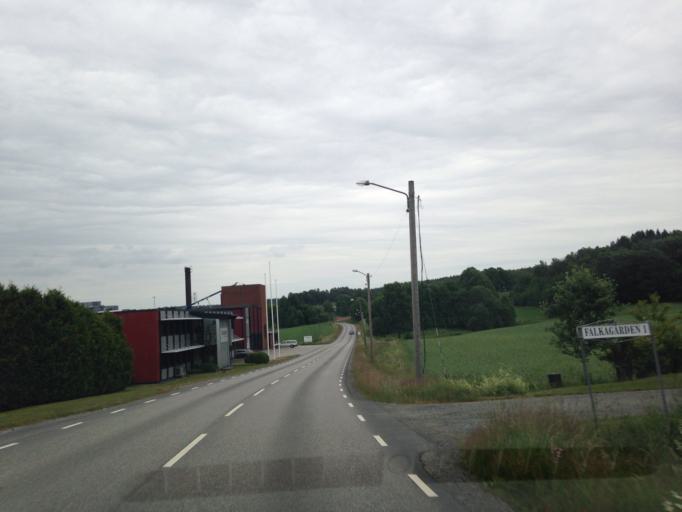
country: SE
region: Vaestra Goetaland
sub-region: Marks Kommun
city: Bua
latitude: 57.4947
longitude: 12.5296
